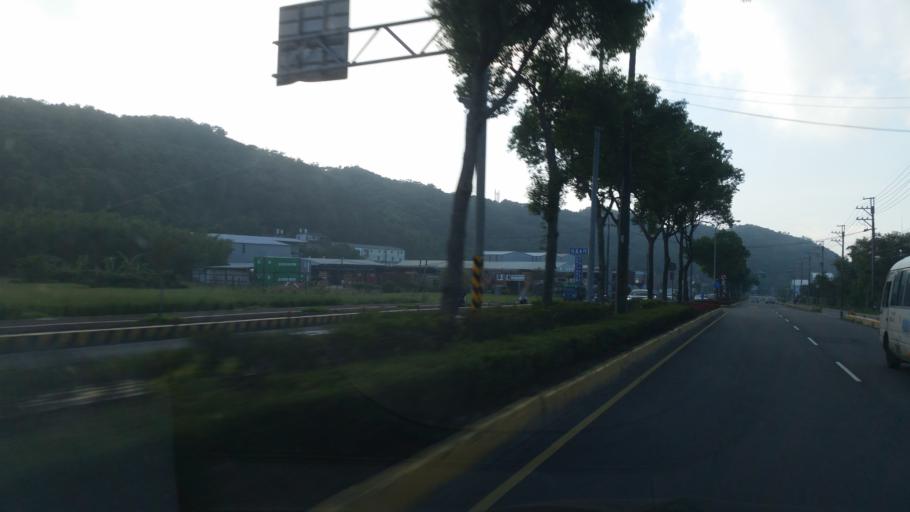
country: TW
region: Taiwan
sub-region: Taoyuan
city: Taoyuan
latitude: 25.0170
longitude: 121.3483
